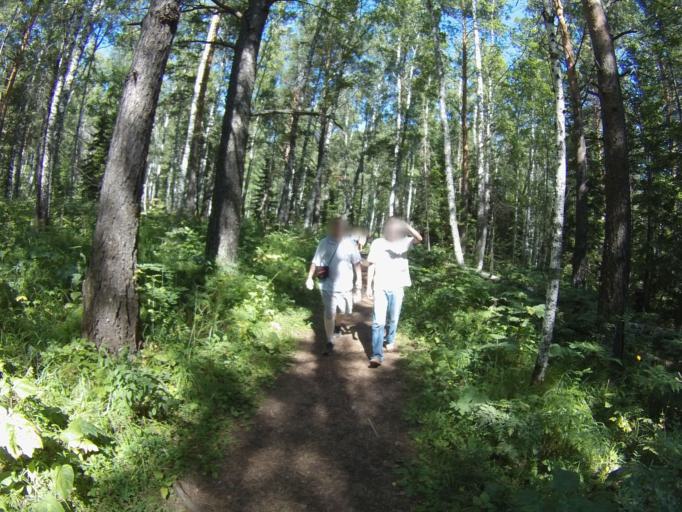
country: RU
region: Krasnoyarskiy
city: Krasnoyarsk
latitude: 55.9445
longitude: 92.7672
